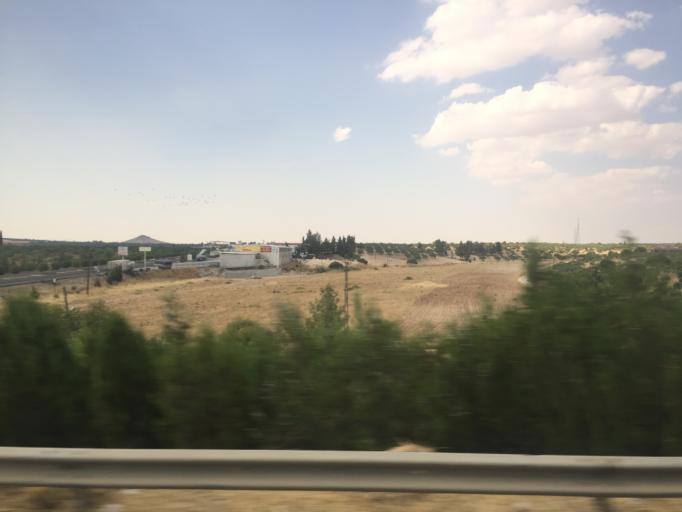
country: TR
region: Sanliurfa
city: Akziyaret
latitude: 37.2695
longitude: 38.7966
